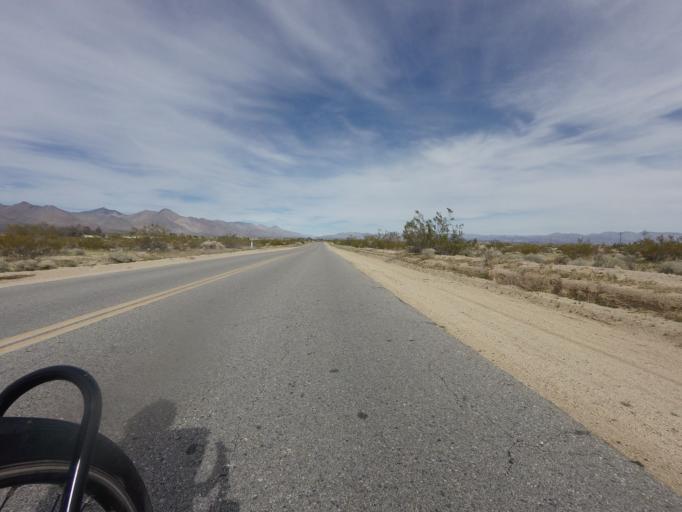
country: US
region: California
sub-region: Kern County
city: Inyokern
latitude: 35.7117
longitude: -117.8318
